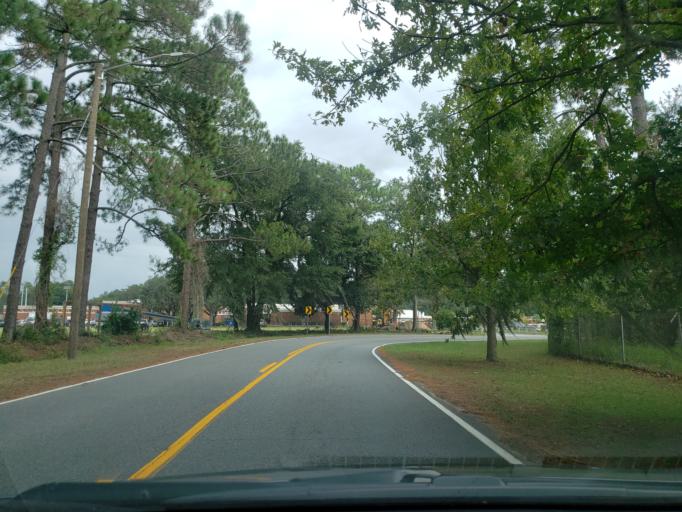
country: US
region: Georgia
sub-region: Chatham County
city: Isle of Hope
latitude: 32.0105
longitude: -81.0950
